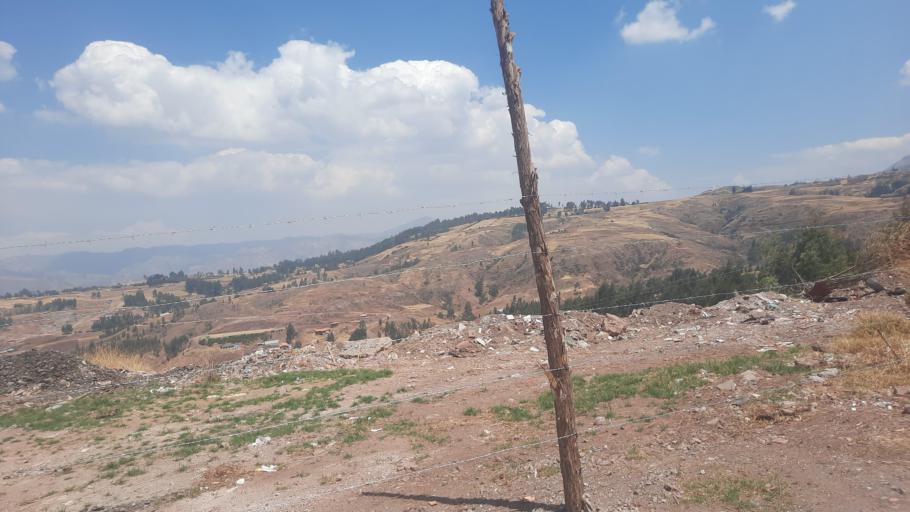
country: PE
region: Cusco
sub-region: Provincia de Cusco
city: Cusco
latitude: -13.4973
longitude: -71.9289
